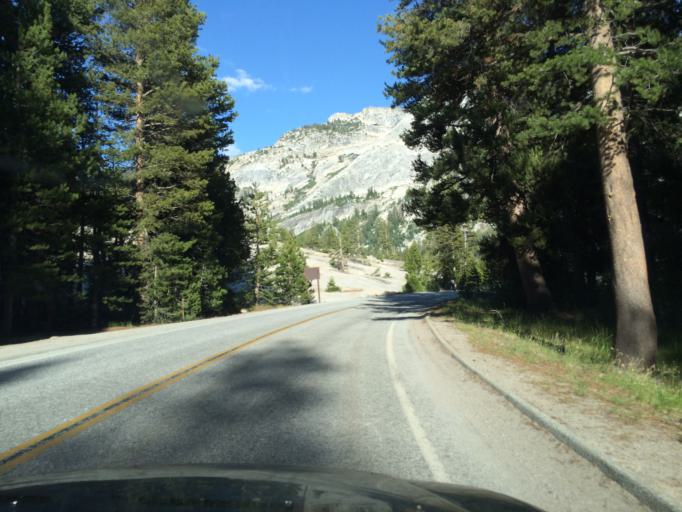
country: US
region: California
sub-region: Mariposa County
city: Yosemite Valley
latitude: 37.8343
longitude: -119.4629
